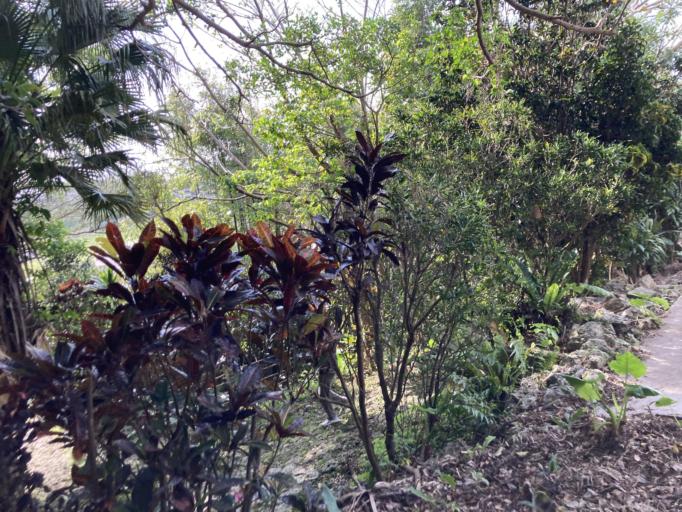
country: JP
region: Okinawa
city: Tomigusuku
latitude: 26.1859
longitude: 127.7569
